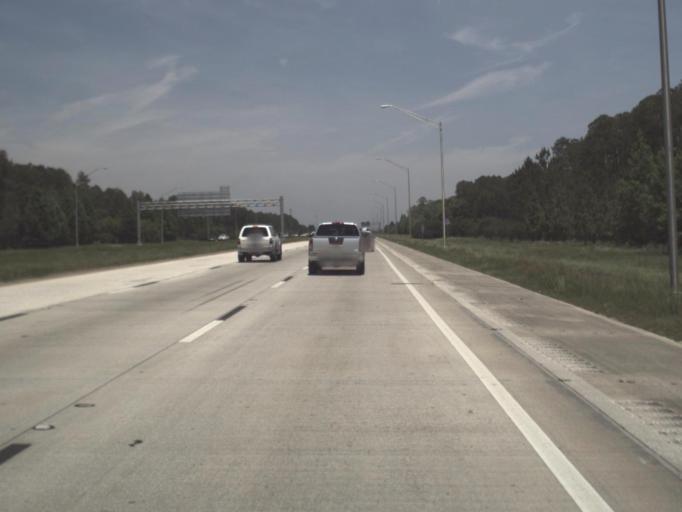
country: US
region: Florida
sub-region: Saint Johns County
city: Palm Valley
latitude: 30.1976
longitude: -81.5136
